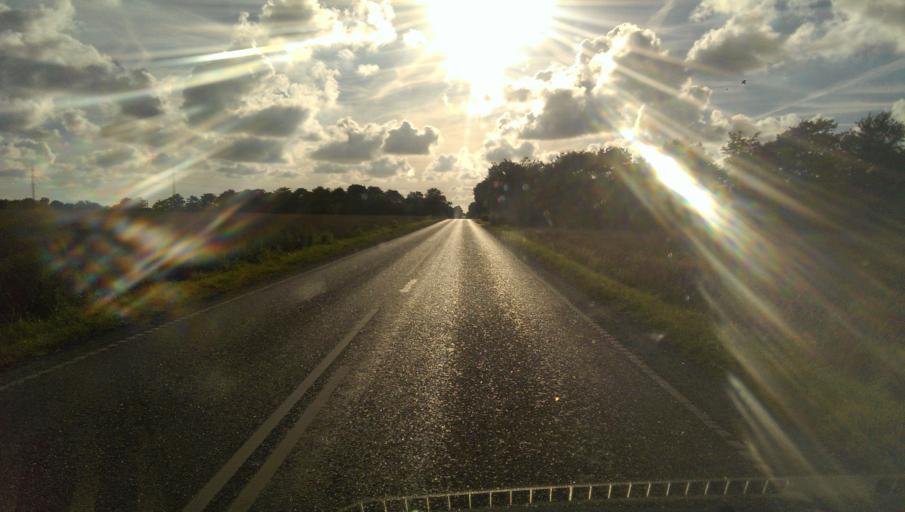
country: DK
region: South Denmark
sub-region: Esbjerg Kommune
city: Esbjerg
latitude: 55.5178
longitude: 8.5076
